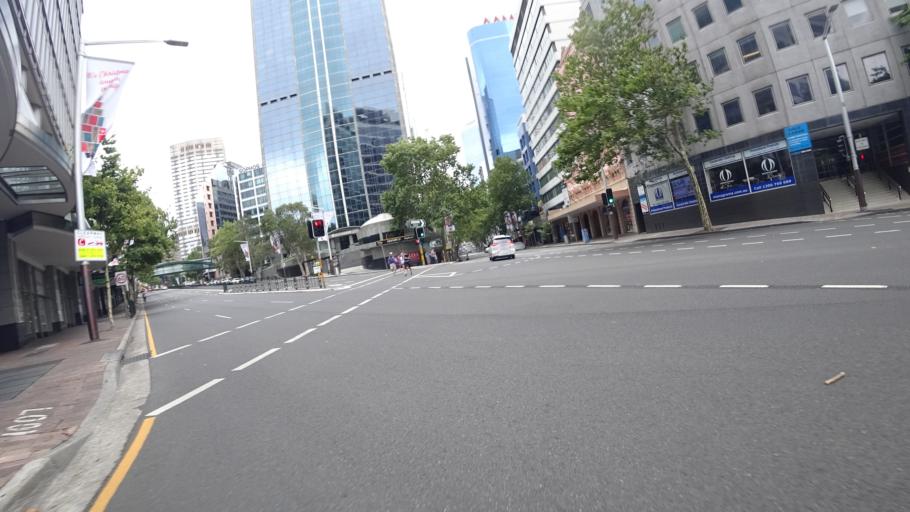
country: AU
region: New South Wales
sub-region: North Sydney
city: North Sydney
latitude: -33.8407
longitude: 151.2084
